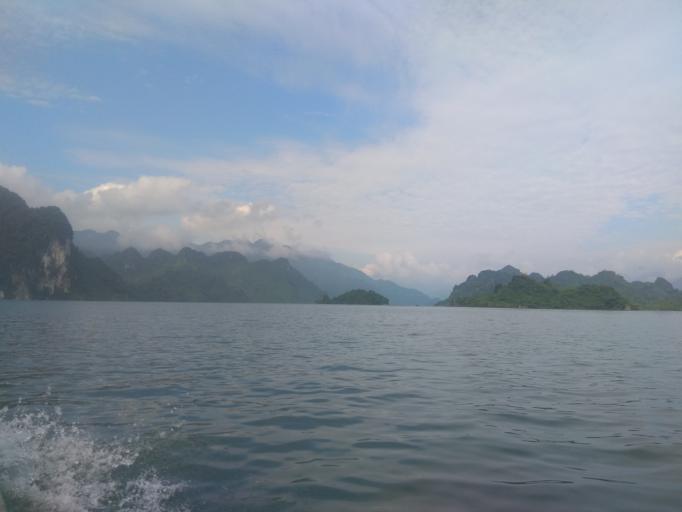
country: VN
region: Hoa Binh
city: Da Bac
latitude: 20.7543
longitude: 105.1475
